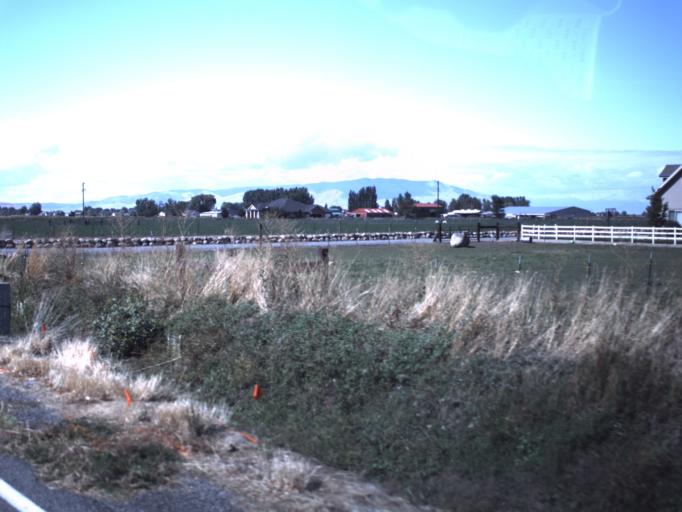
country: US
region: Utah
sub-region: Utah County
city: Benjamin
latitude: 40.1148
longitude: -111.7043
